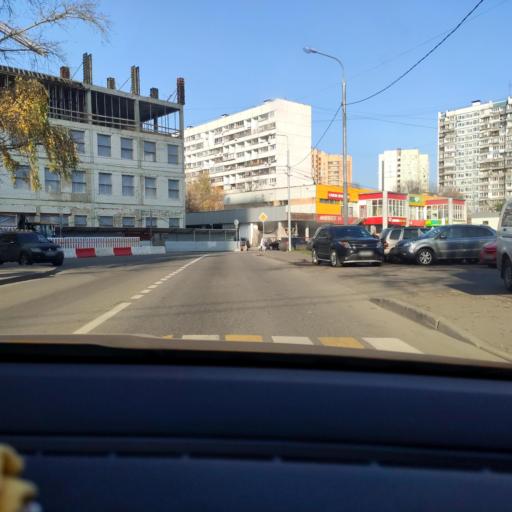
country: RU
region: Moscow
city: Vatutino
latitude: 55.8800
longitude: 37.6936
